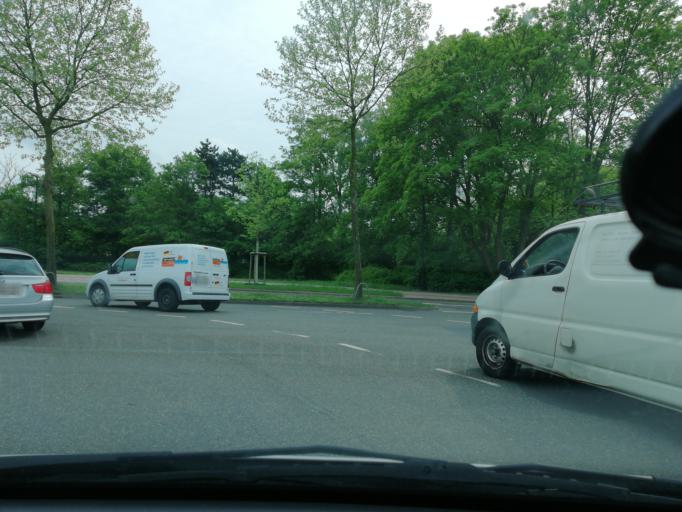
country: DE
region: North Rhine-Westphalia
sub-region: Regierungsbezirk Dusseldorf
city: Dusseldorf
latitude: 51.2010
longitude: 6.7541
